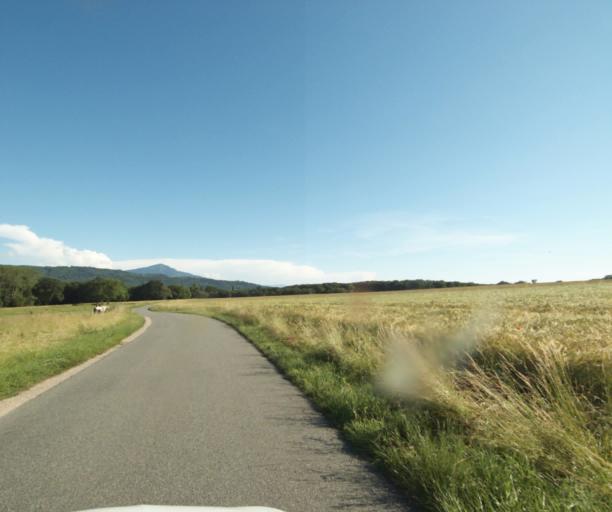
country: FR
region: Rhone-Alpes
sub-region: Departement de la Haute-Savoie
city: Massongy
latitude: 46.3447
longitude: 6.3281
